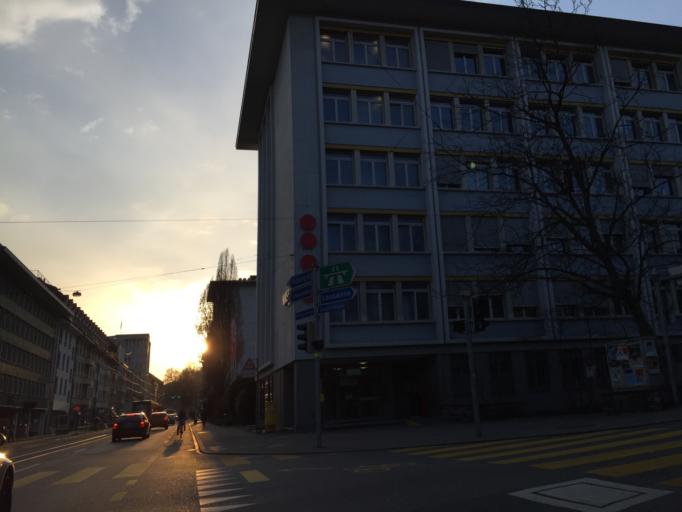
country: CH
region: Bern
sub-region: Bern-Mittelland District
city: Bern
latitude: 46.9458
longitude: 7.4294
